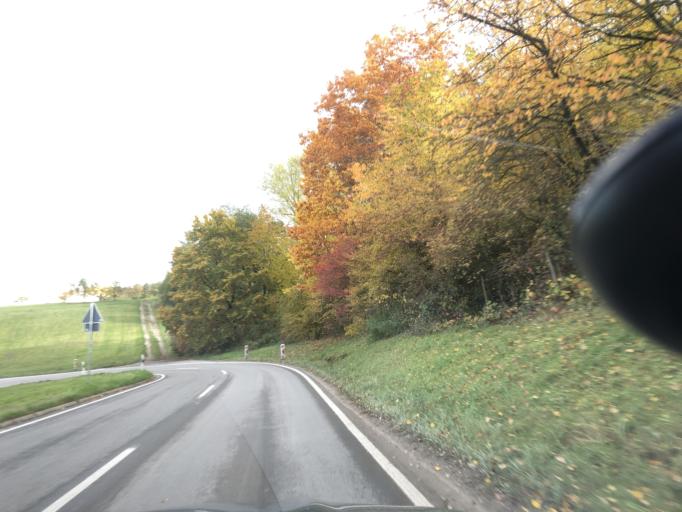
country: DE
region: Baden-Wuerttemberg
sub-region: Regierungsbezirk Stuttgart
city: Winterbach
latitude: 48.8256
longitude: 9.4657
